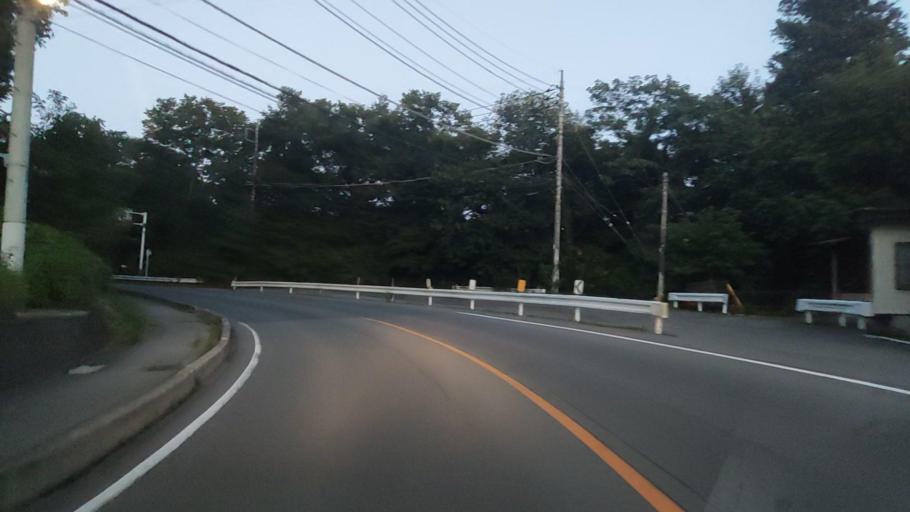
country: JP
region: Gunma
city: Nakanojomachi
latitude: 36.5526
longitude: 138.6125
